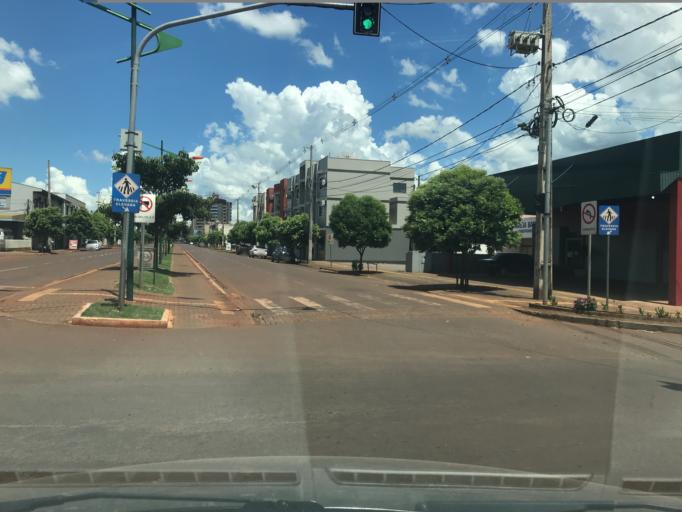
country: BR
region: Parana
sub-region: Palotina
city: Palotina
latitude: -24.2780
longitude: -53.8417
